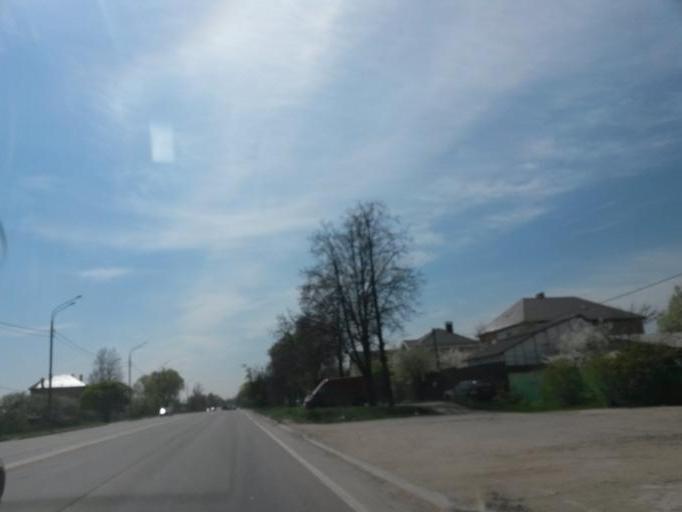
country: RU
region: Moskovskaya
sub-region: Podol'skiy Rayon
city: Podol'sk
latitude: 55.3951
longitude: 37.5472
